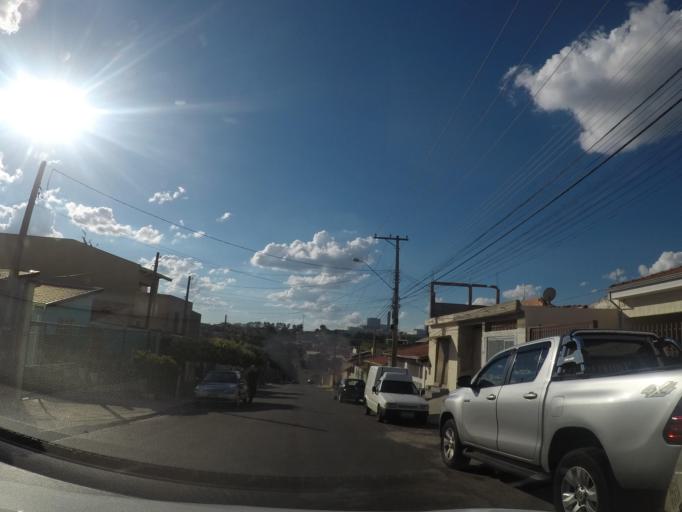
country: BR
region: Sao Paulo
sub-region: Sumare
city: Sumare
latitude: -22.8088
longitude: -47.2288
